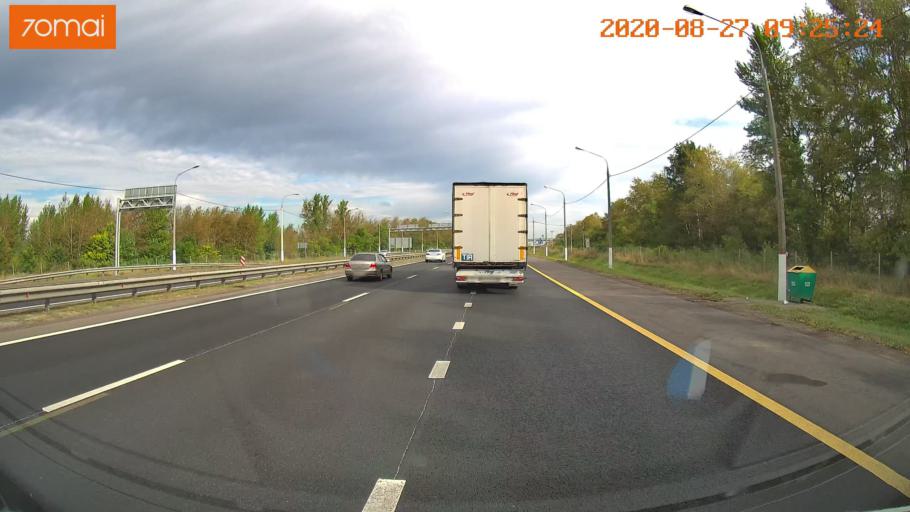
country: RU
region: Tula
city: Kazachka
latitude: 53.2936
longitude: 38.1783
